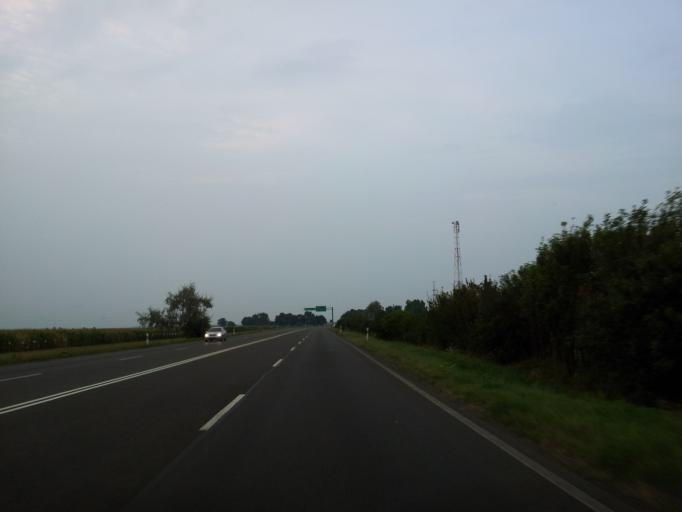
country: HU
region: Tolna
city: Szekszard
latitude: 46.3992
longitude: 18.7156
